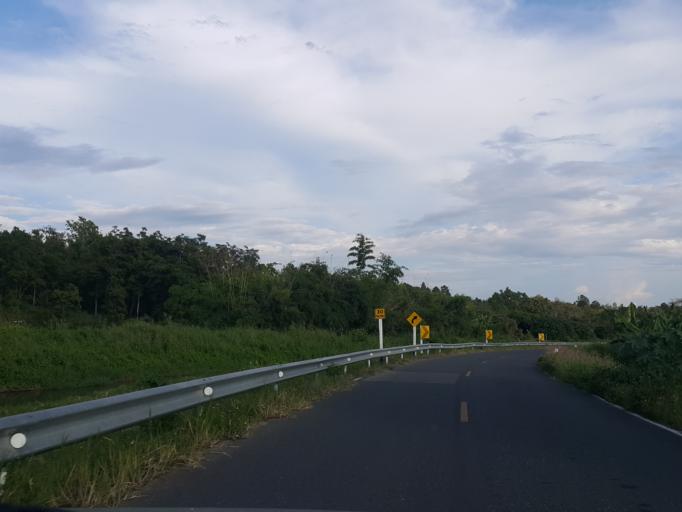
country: TH
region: Chiang Mai
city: San Sai
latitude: 18.9669
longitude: 98.9905
